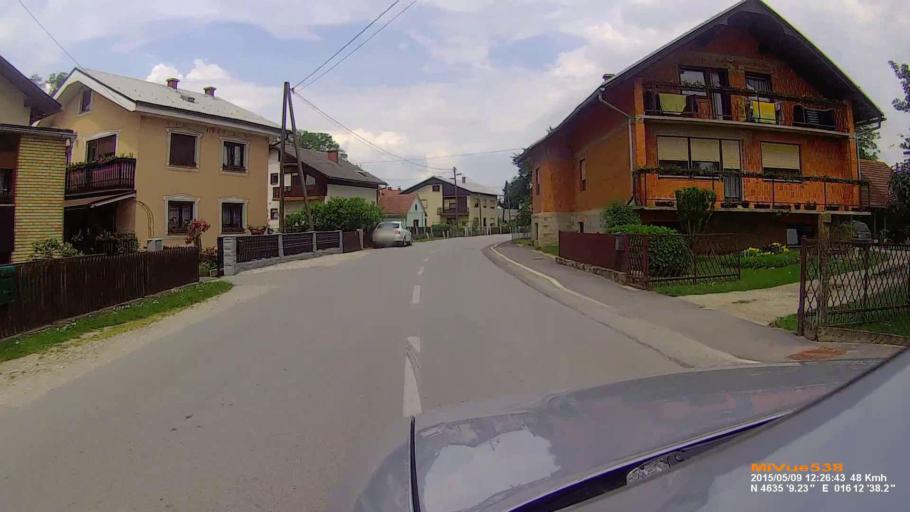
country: SI
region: Beltinci
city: Beltinci
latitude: 46.5860
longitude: 16.2106
